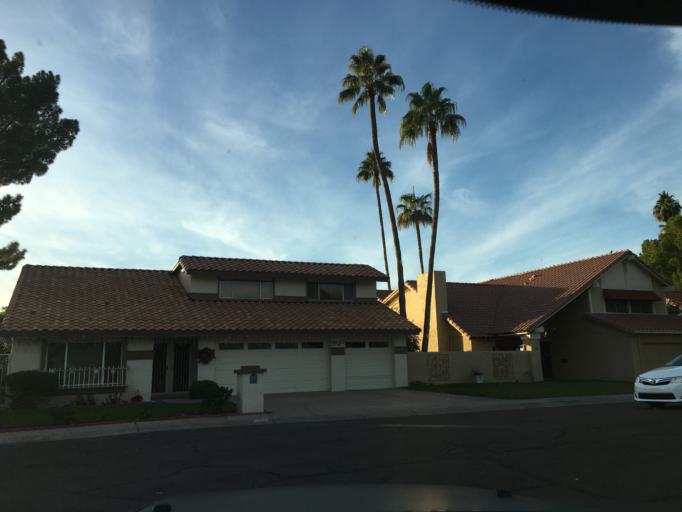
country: US
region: Arizona
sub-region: Maricopa County
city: Tempe
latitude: 33.3747
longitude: -111.9141
